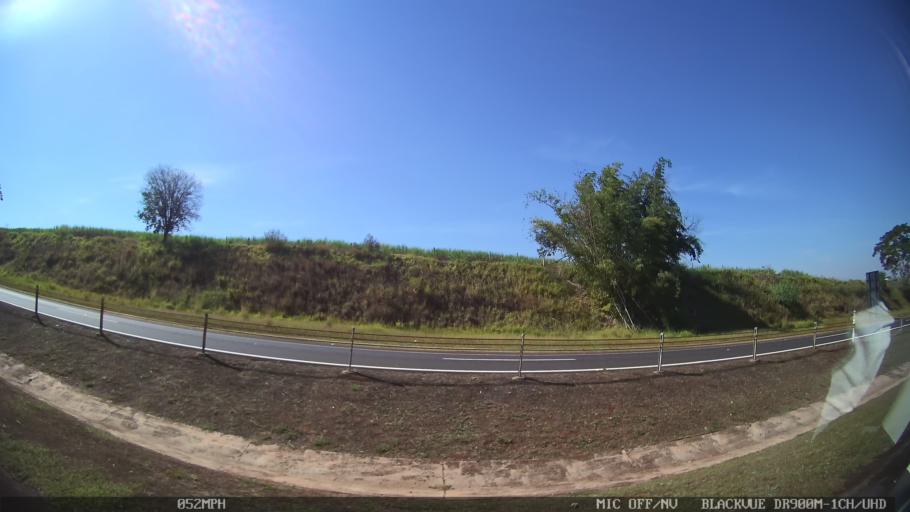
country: BR
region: Sao Paulo
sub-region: Ribeirao Preto
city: Ribeirao Preto
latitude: -21.1925
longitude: -47.8852
